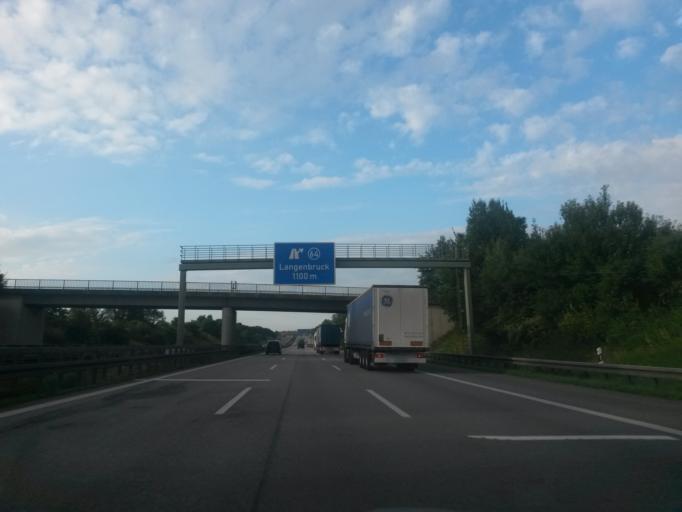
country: DE
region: Bavaria
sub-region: Upper Bavaria
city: Reichertshofen
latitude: 48.6594
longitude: 11.5119
